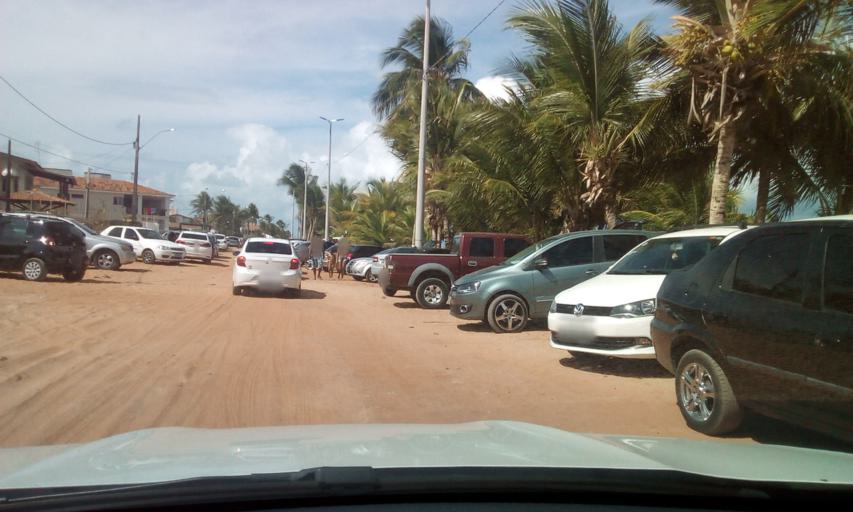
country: BR
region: Paraiba
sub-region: Cabedelo
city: Cabedelo
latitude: -6.9825
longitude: -34.8280
